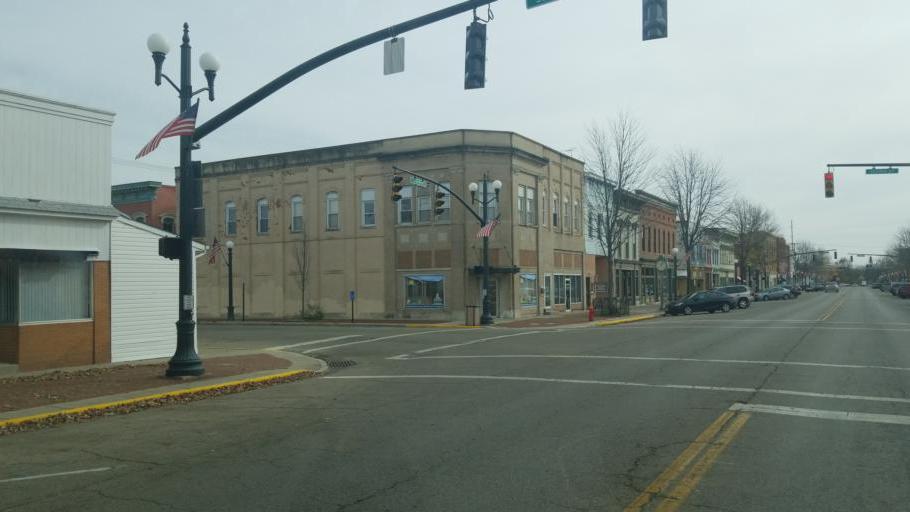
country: US
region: Ohio
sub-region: Madison County
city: London
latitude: 39.8858
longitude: -83.4479
